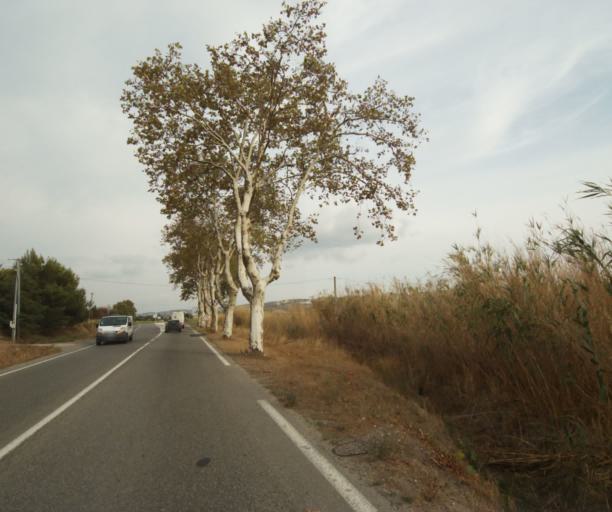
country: FR
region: Provence-Alpes-Cote d'Azur
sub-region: Departement des Bouches-du-Rhone
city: Gignac-la-Nerthe
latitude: 43.3950
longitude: 5.2169
